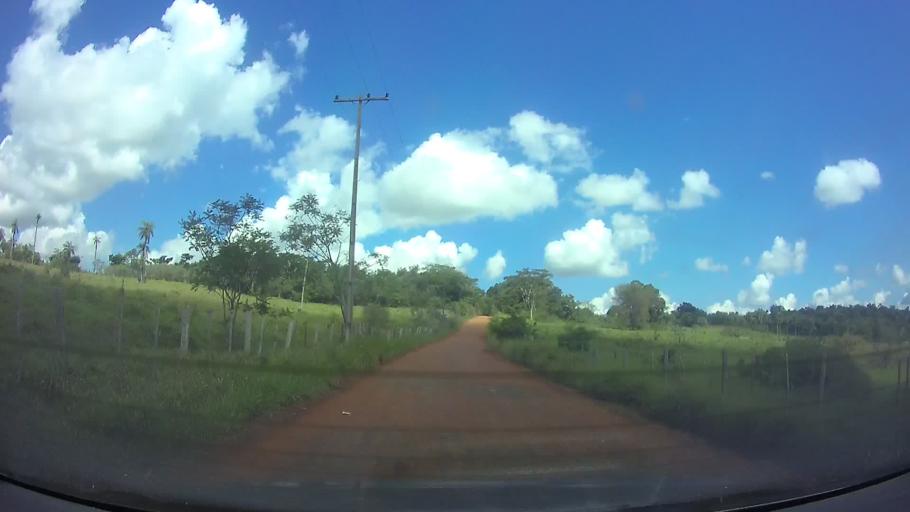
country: PY
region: Paraguari
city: La Colmena
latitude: -25.9386
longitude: -56.7808
